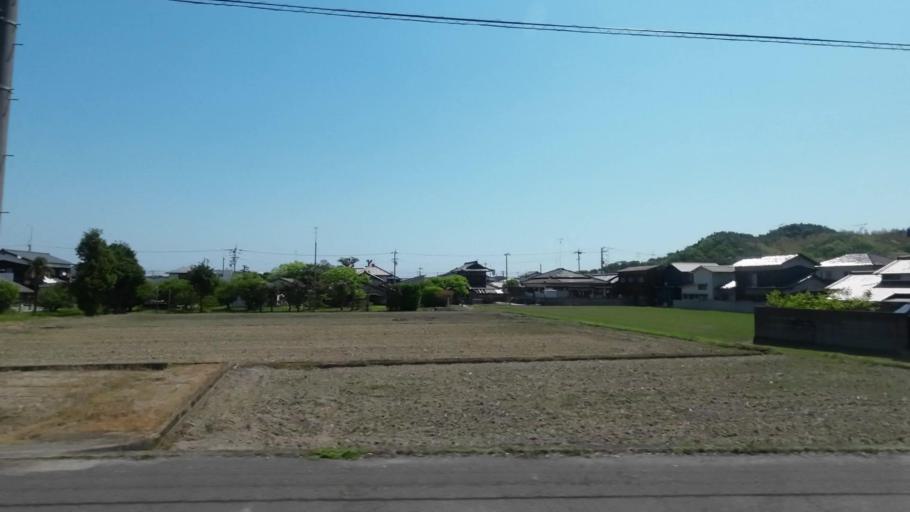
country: JP
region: Ehime
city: Saijo
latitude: 34.0139
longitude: 133.0351
